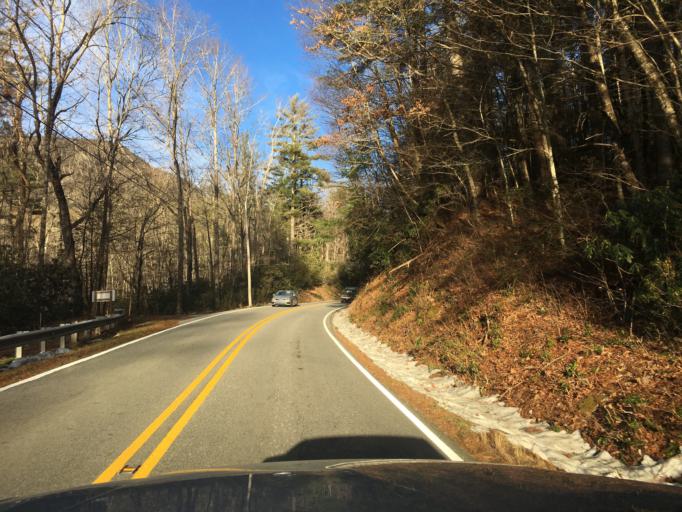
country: US
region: North Carolina
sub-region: Jackson County
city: Cullowhee
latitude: 35.1149
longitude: -82.9866
